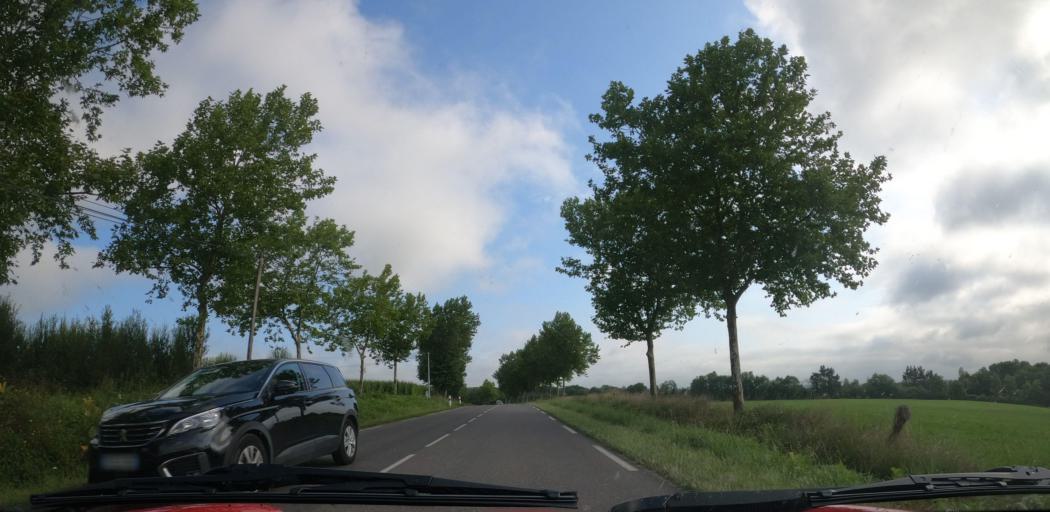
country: FR
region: Aquitaine
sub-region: Departement des Landes
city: Peyrehorade
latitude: 43.5231
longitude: -1.1047
